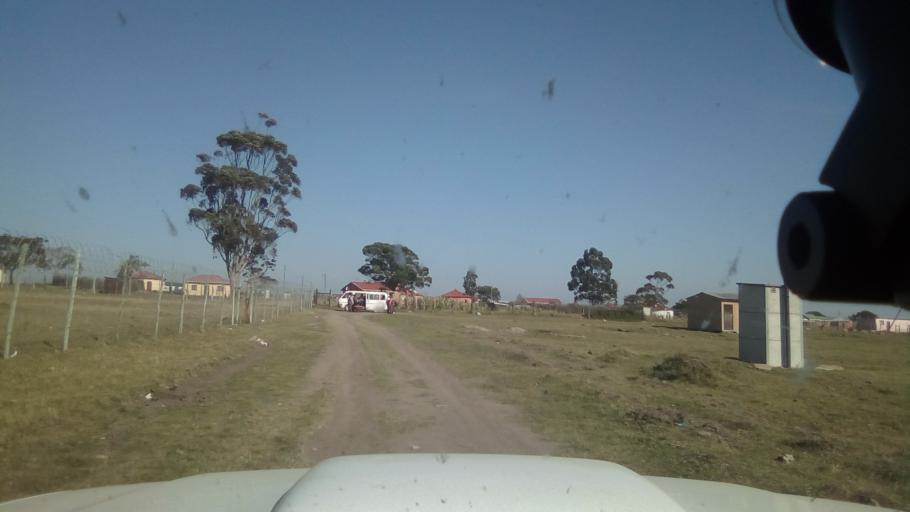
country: ZA
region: Eastern Cape
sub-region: Buffalo City Metropolitan Municipality
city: Bhisho
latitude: -32.9400
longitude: 27.3346
